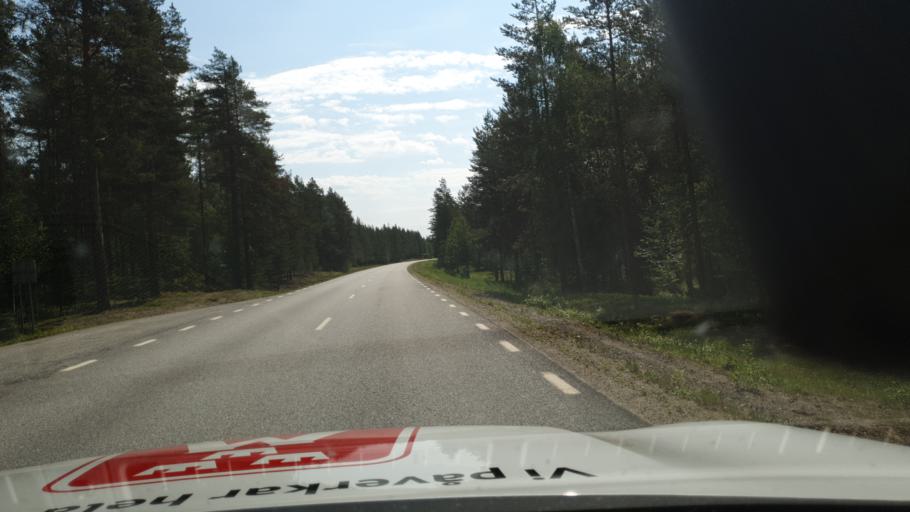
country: SE
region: Vaesterbotten
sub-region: Vindelns Kommun
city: Vindeln
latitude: 64.3718
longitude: 19.4192
